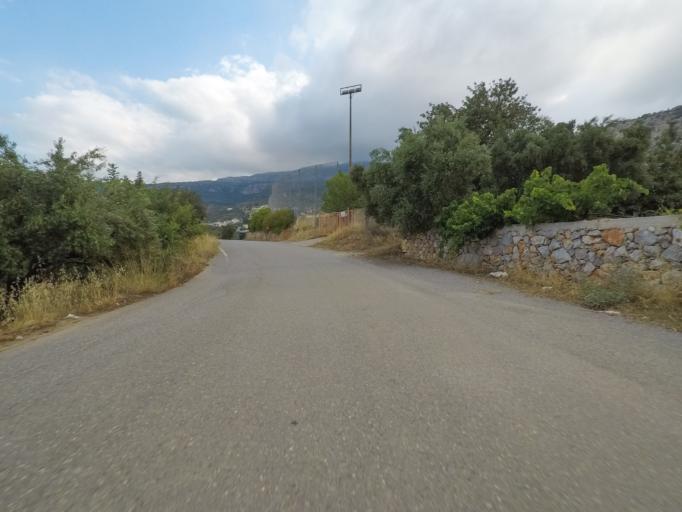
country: GR
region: Crete
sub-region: Nomos Lasithiou
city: Kritsa
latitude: 35.1612
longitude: 25.6505
